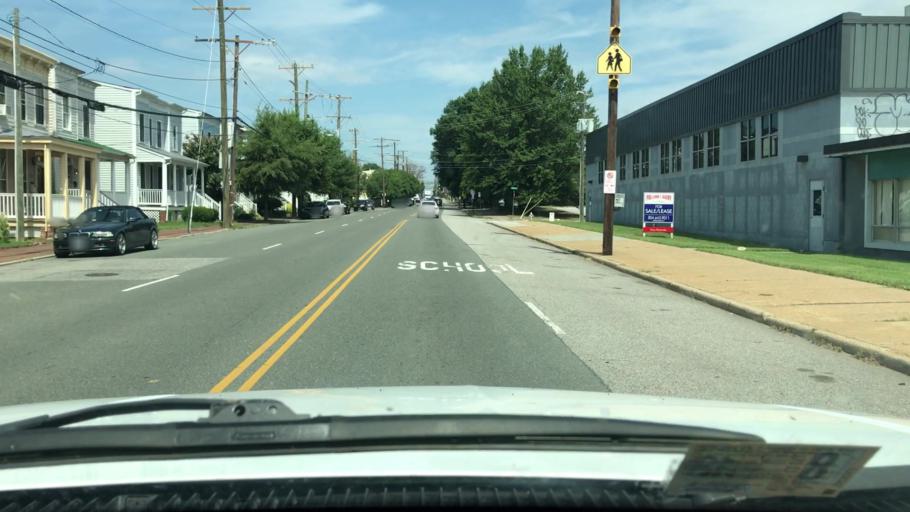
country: US
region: Virginia
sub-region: City of Richmond
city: Richmond
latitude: 37.5533
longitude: -77.4472
